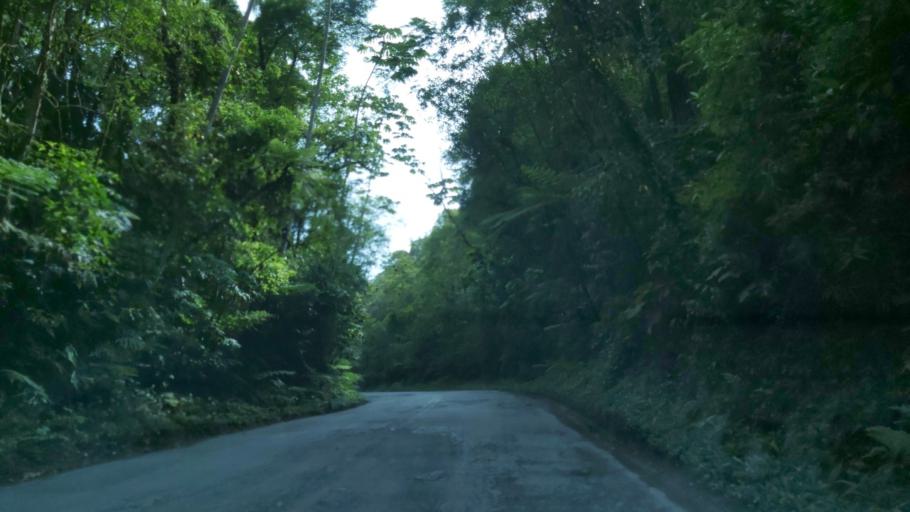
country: BR
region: Sao Paulo
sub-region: Miracatu
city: Miracatu
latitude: -24.0330
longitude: -47.5597
